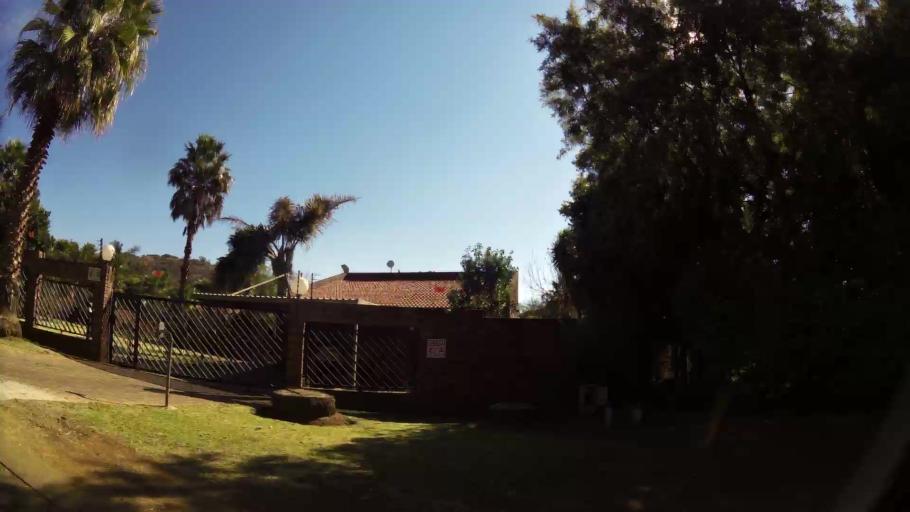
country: ZA
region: Gauteng
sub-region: Ekurhuleni Metropolitan Municipality
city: Germiston
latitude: -26.2882
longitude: 28.0970
